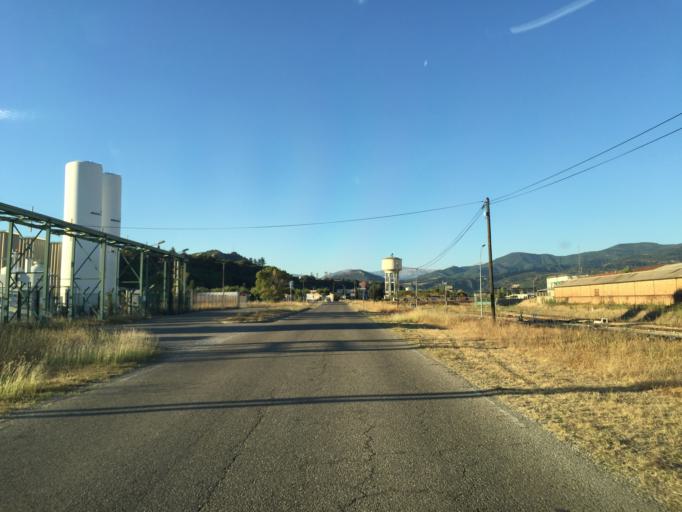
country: FR
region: Provence-Alpes-Cote d'Azur
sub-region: Departement des Alpes-de-Haute-Provence
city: Malijai
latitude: 44.0640
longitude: 5.9981
